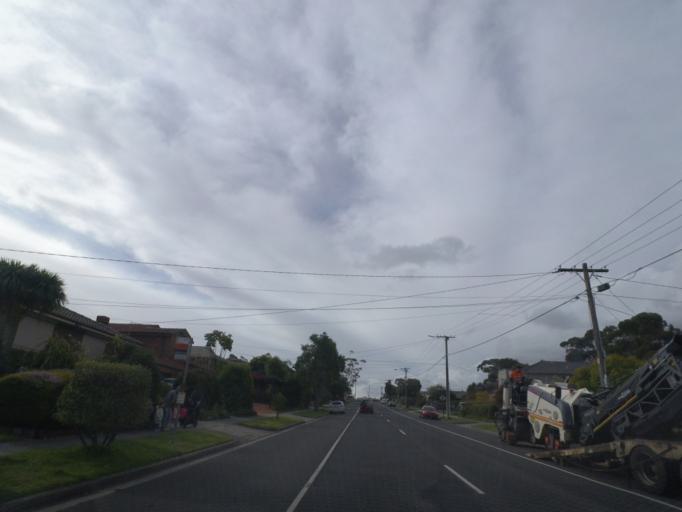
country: AU
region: Victoria
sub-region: Whitehorse
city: Vermont South
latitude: -37.8588
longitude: 145.1826
